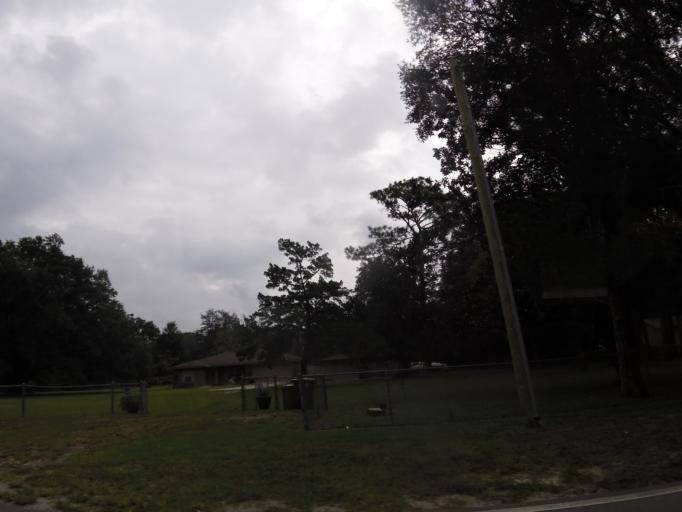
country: US
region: Florida
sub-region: Clay County
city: Bellair-Meadowbrook Terrace
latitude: 30.2320
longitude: -81.7730
